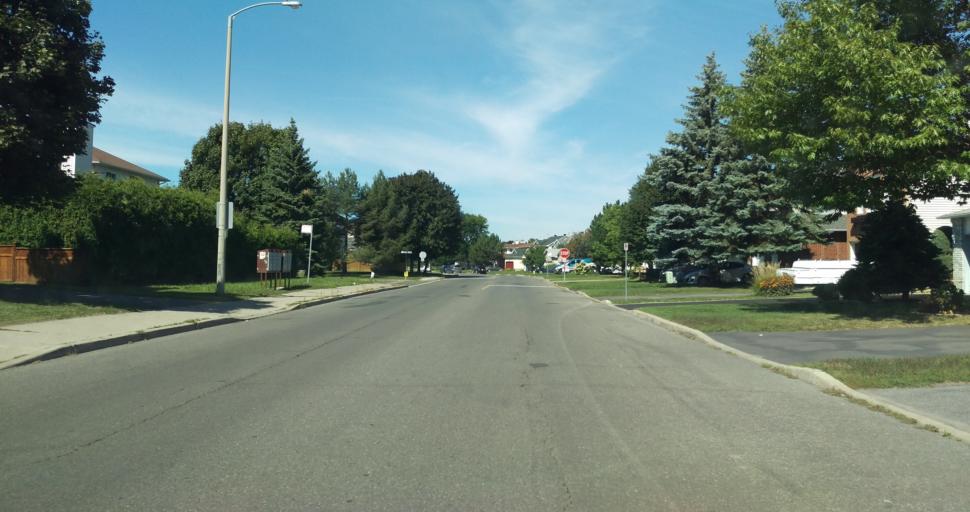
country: CA
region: Ontario
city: Clarence-Rockland
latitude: 45.4687
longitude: -75.4790
